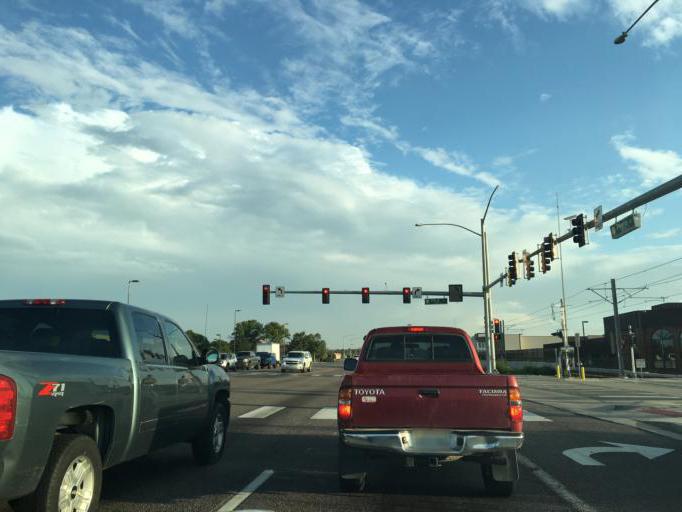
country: US
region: Colorado
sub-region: Adams County
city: Aurora
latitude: 39.7642
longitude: -104.8471
